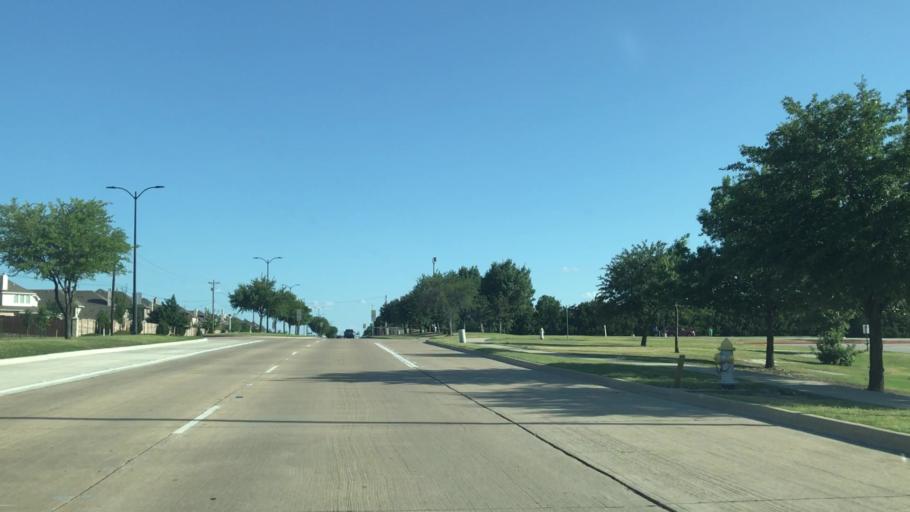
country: US
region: Texas
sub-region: Collin County
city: Frisco
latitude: 33.1359
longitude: -96.7681
